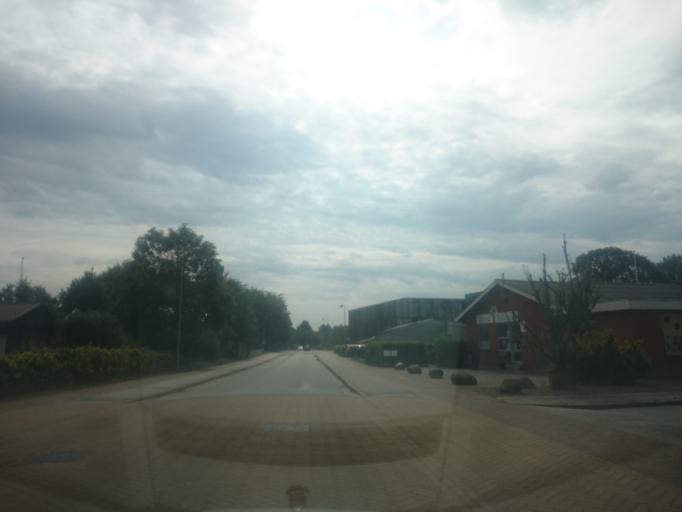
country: DK
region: South Denmark
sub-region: Billund Kommune
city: Billund
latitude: 55.7344
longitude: 9.1158
